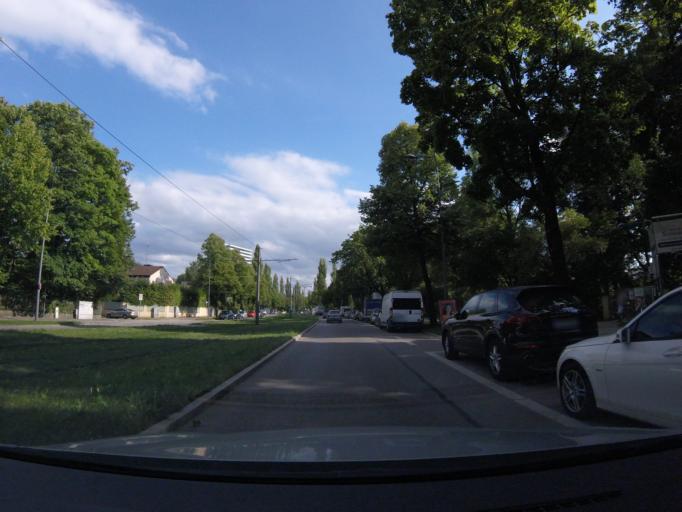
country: DE
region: Bavaria
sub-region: Upper Bavaria
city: Bogenhausen
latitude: 48.1582
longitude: 11.6289
